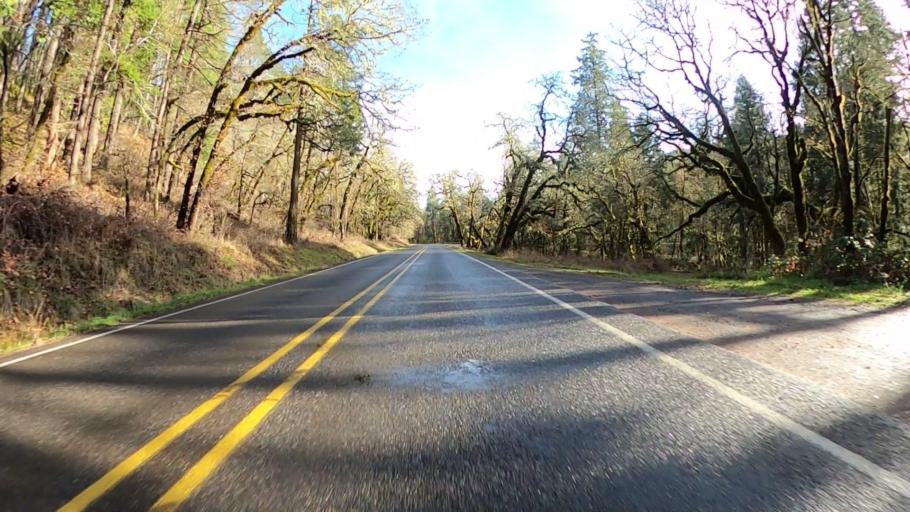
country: US
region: Oregon
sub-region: Lane County
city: Oakridge
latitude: 43.7483
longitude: -122.5095
